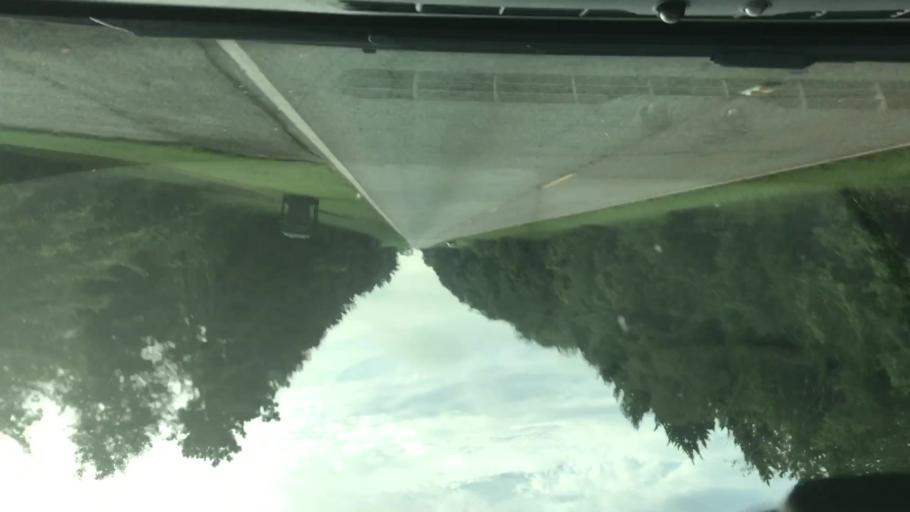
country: US
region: Georgia
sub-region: Quitman County
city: Georgetown
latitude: 31.8988
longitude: -85.0497
